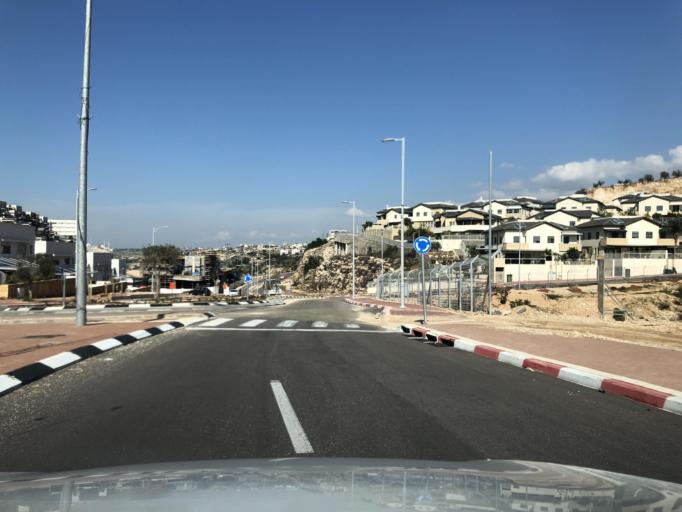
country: PS
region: West Bank
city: Mashah
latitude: 32.1117
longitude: 35.0427
